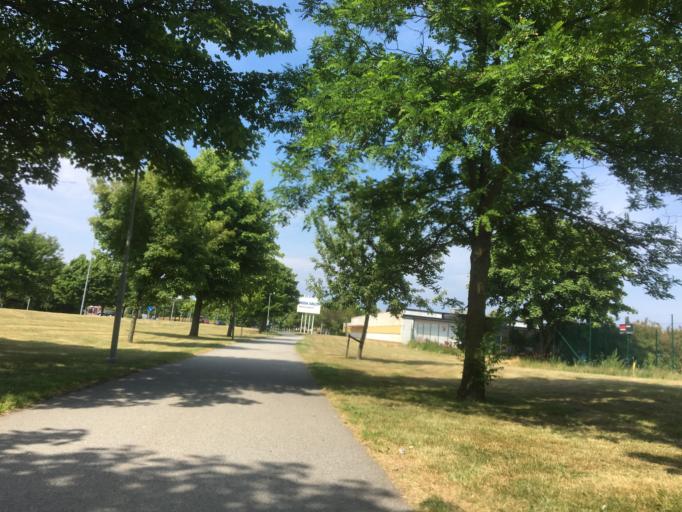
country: SE
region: Skane
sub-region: Landskrona
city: Landskrona
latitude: 55.8838
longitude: 12.8473
